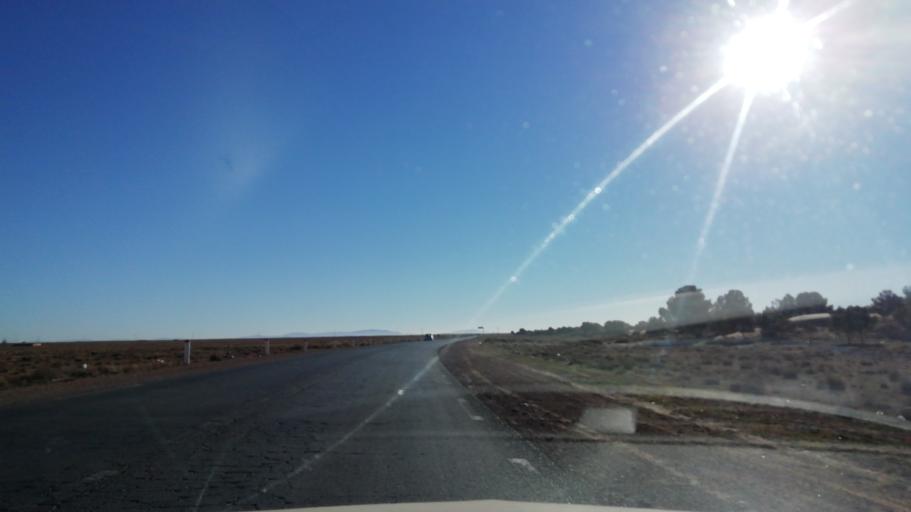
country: DZ
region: El Bayadh
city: El Bayadh
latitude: 33.8516
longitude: 0.6585
